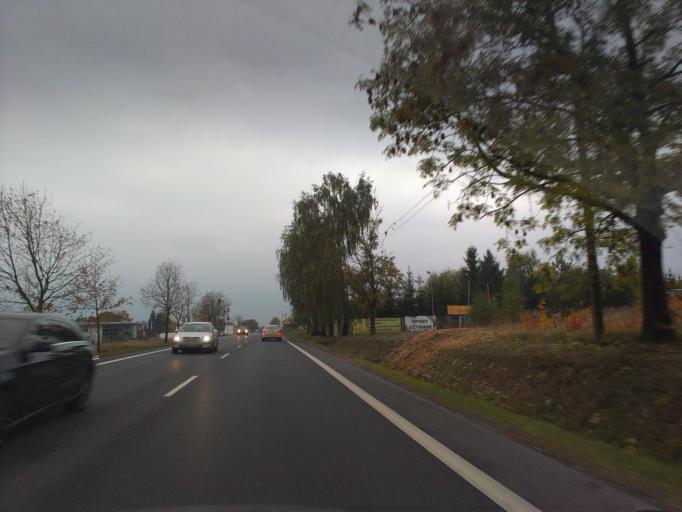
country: PL
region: Greater Poland Voivodeship
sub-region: Powiat poznanski
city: Suchy Las
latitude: 52.4806
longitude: 16.8646
